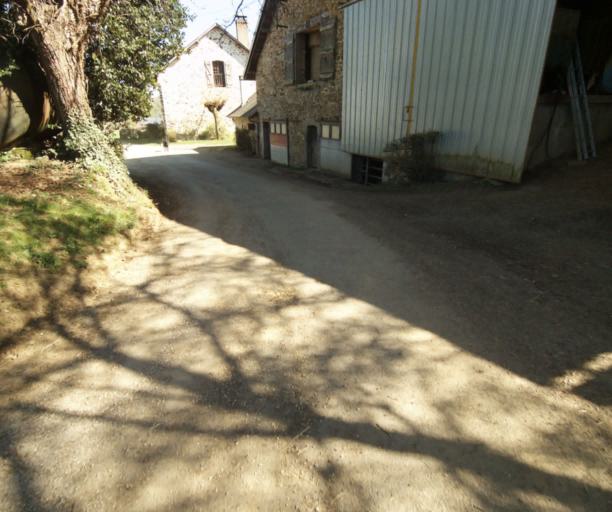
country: FR
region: Limousin
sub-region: Departement de la Correze
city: Chamboulive
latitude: 45.4202
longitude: 1.6624
